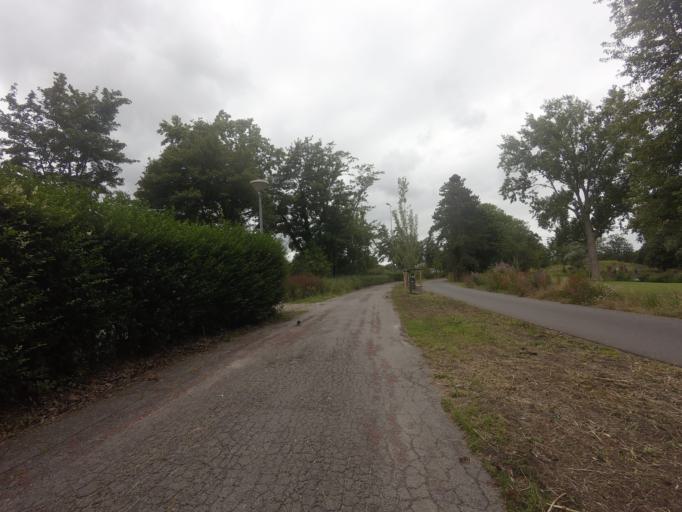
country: NL
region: North Holland
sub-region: Gemeente Bloemendaal
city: Bloemendaal
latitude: 52.4115
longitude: 4.6447
